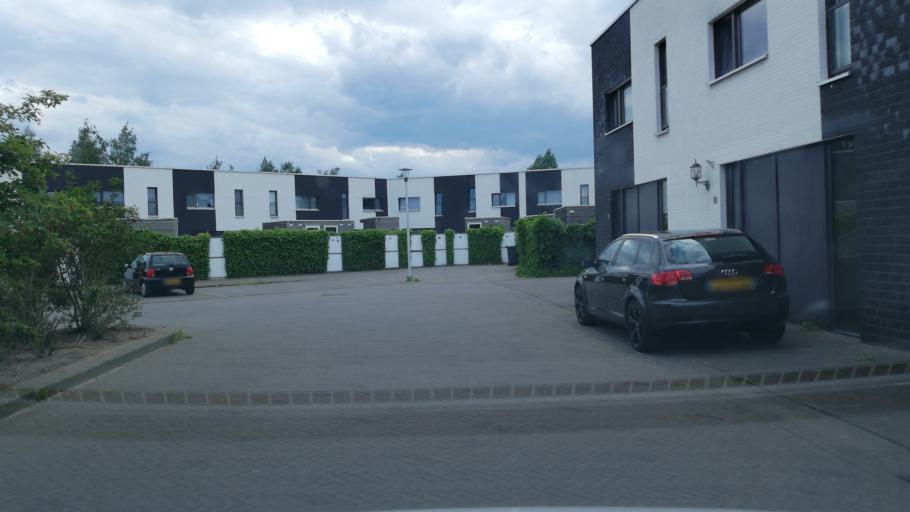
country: NL
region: Gelderland
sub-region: Gemeente Apeldoorn
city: Apeldoorn
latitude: 52.2410
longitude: 5.9930
